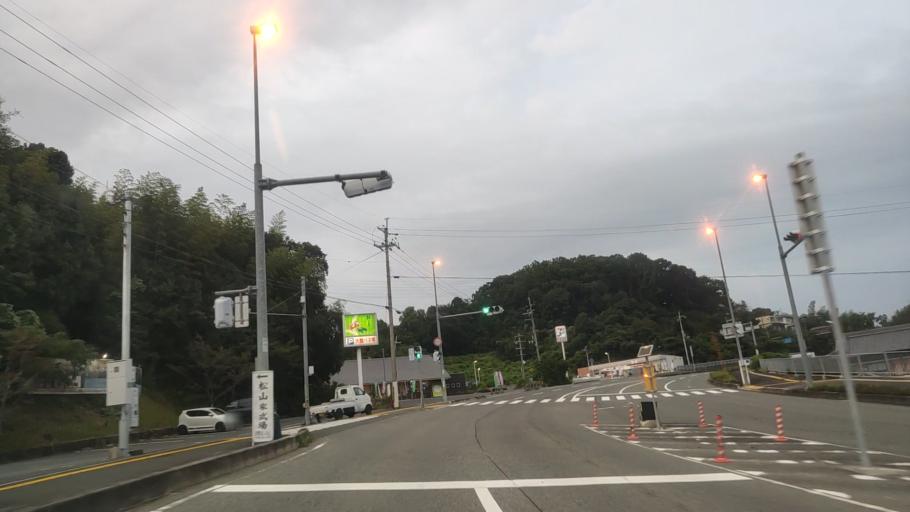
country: JP
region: Wakayama
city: Hashimoto
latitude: 34.3170
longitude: 135.6020
